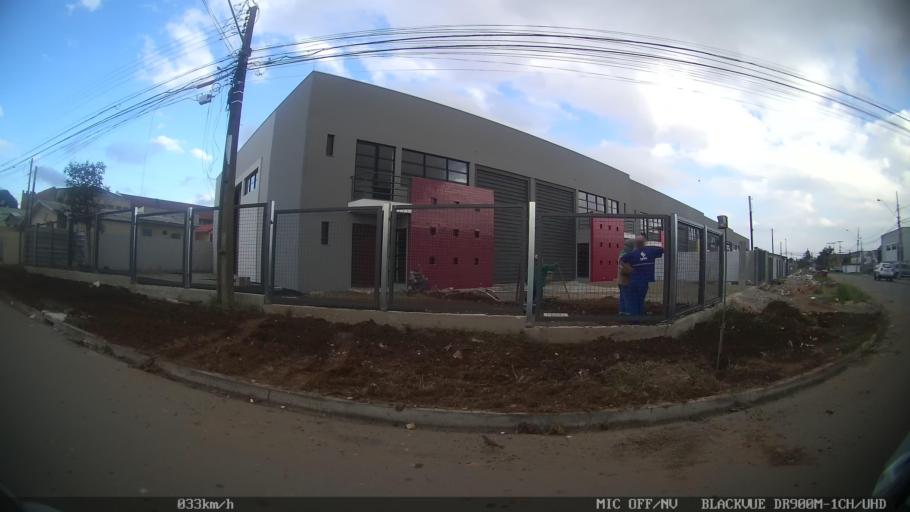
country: BR
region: Parana
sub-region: Pinhais
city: Pinhais
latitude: -25.4358
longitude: -49.1952
